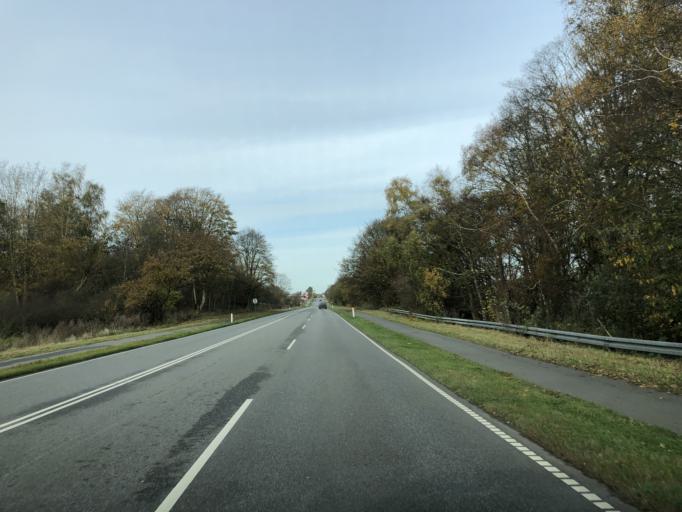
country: DK
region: Capital Region
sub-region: Allerod Kommune
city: Blovstrod
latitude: 55.8603
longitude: 12.3969
